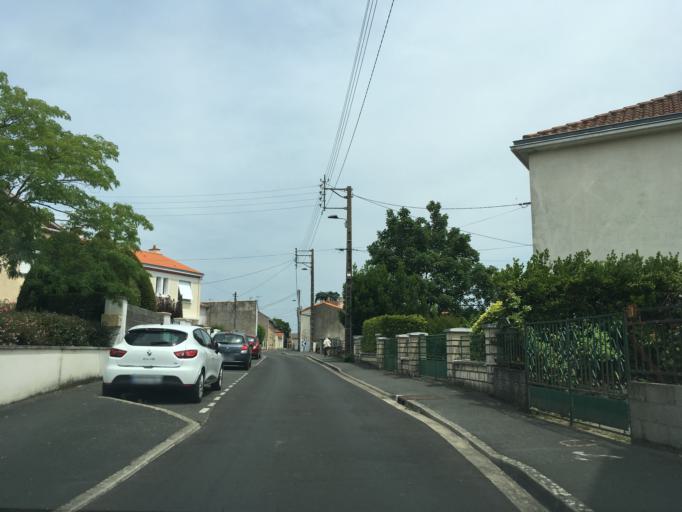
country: FR
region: Poitou-Charentes
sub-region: Departement des Deux-Sevres
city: Niort
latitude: 46.3206
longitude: -0.4779
